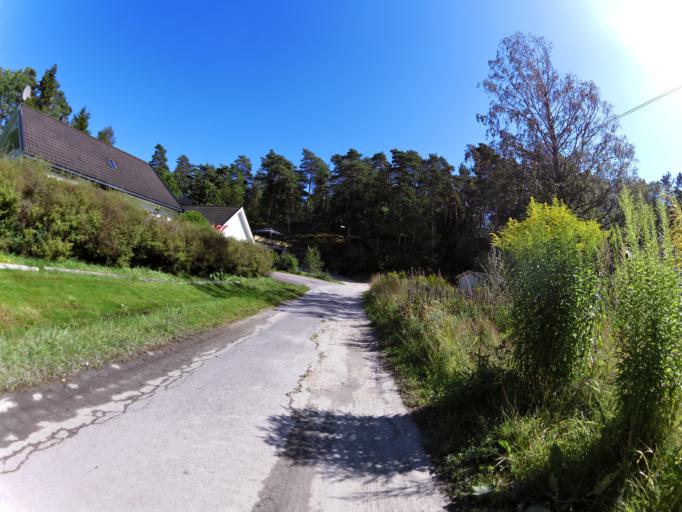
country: NO
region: Ostfold
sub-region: Fredrikstad
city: Fredrikstad
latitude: 59.1783
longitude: 10.8457
